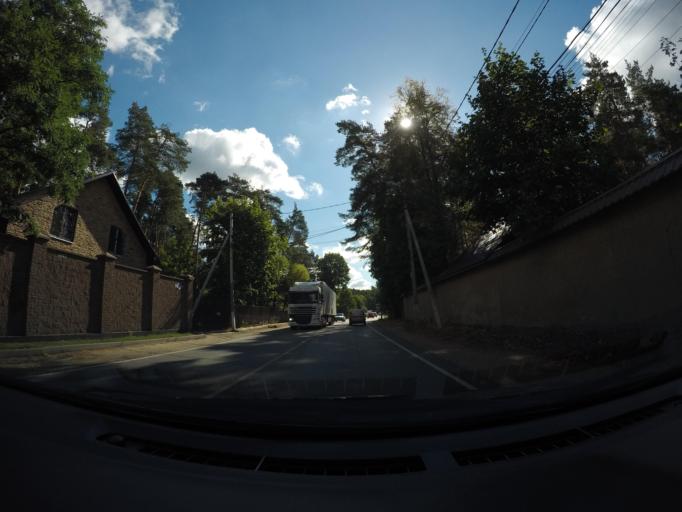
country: RU
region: Moskovskaya
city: Kratovo
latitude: 55.6044
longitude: 38.1493
